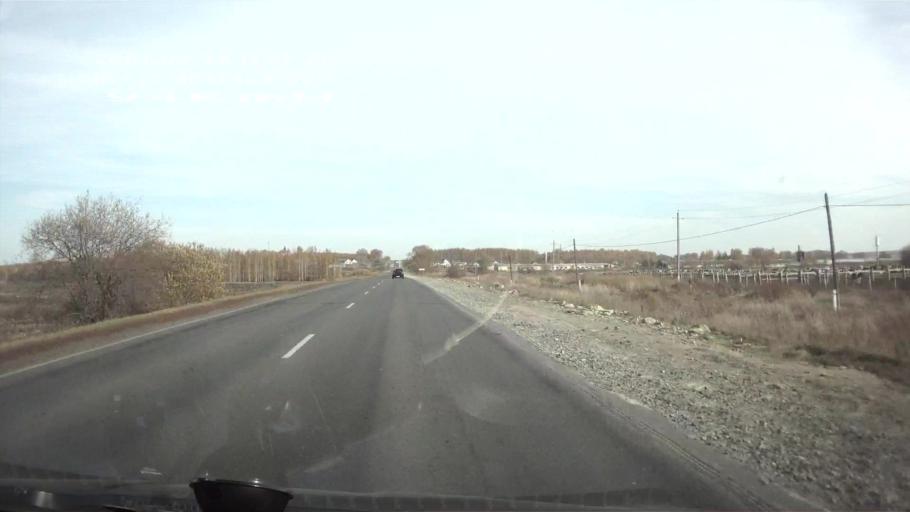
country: RU
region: Mordoviya
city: Atyashevo
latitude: 54.5572
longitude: 45.9700
